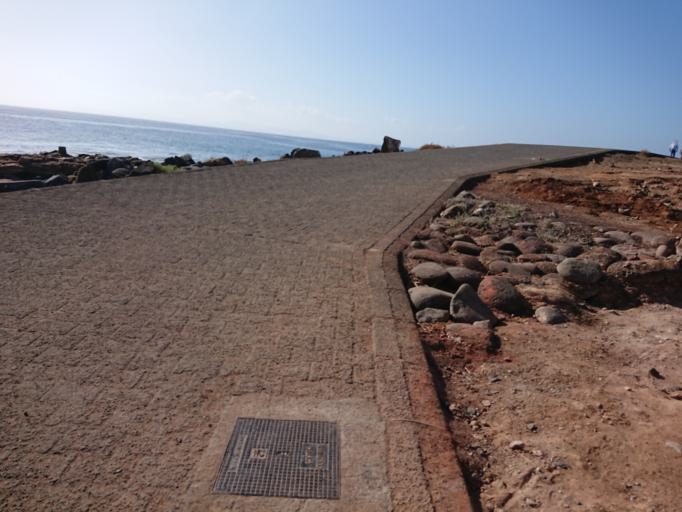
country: ES
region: Canary Islands
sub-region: Provincia de Las Palmas
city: Playa Blanca
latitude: 28.8594
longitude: -13.8653
